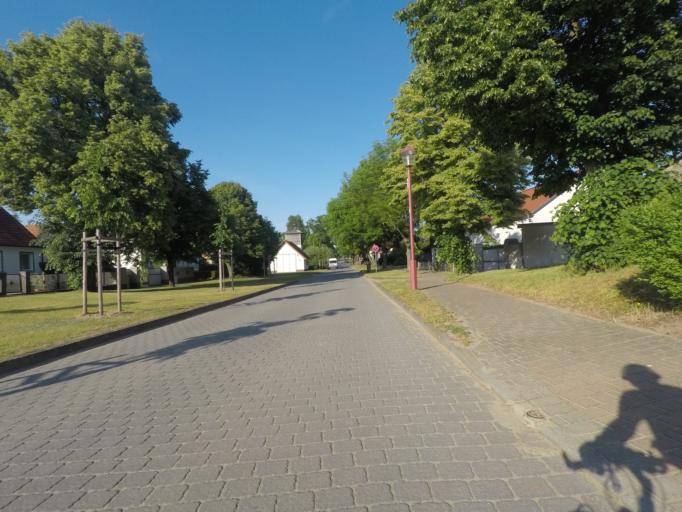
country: DE
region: Brandenburg
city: Joachimsthal
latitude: 52.8895
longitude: 13.7014
